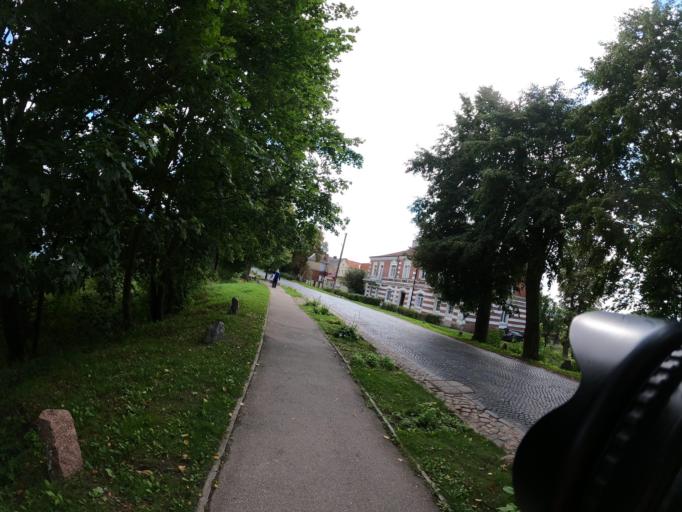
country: RU
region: Kaliningrad
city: Zheleznodorozhnyy
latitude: 54.3574
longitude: 21.3068
